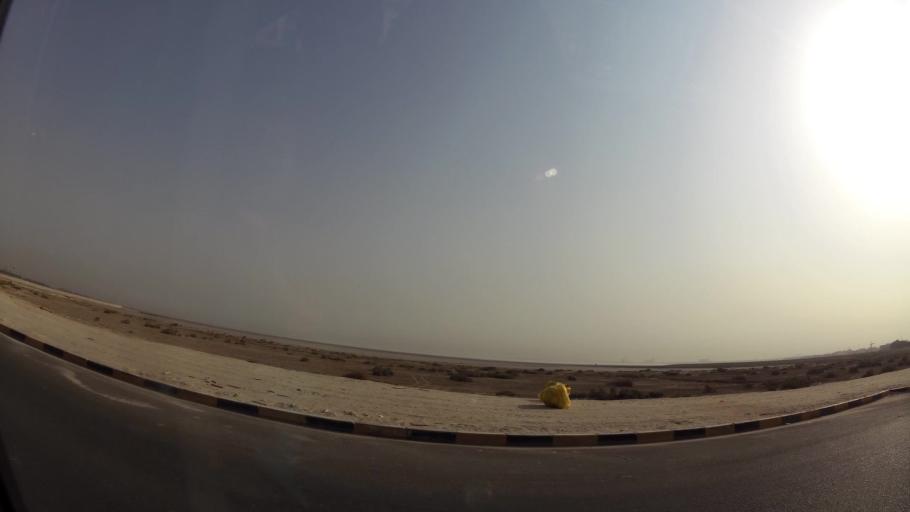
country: KW
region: Al Asimah
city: Ar Rabiyah
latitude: 29.3262
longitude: 47.8180
